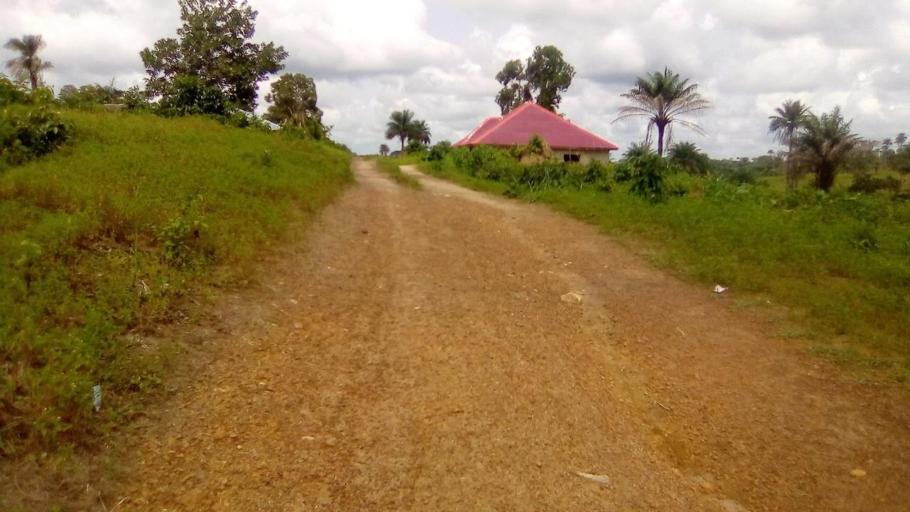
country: SL
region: Southern Province
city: Bo
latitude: 7.9284
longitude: -11.7481
